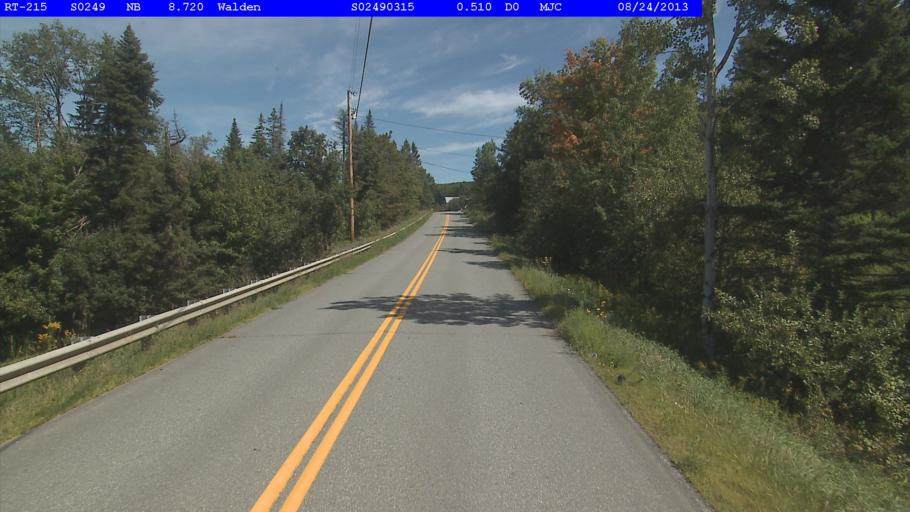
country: US
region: Vermont
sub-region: Caledonia County
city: Hardwick
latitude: 44.4476
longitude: -72.2619
